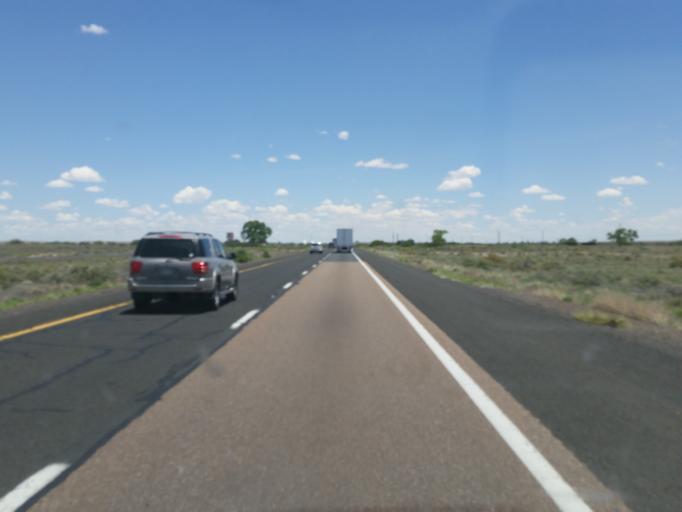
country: US
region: Arizona
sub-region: Navajo County
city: Joseph City
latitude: 34.9657
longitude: -110.4124
